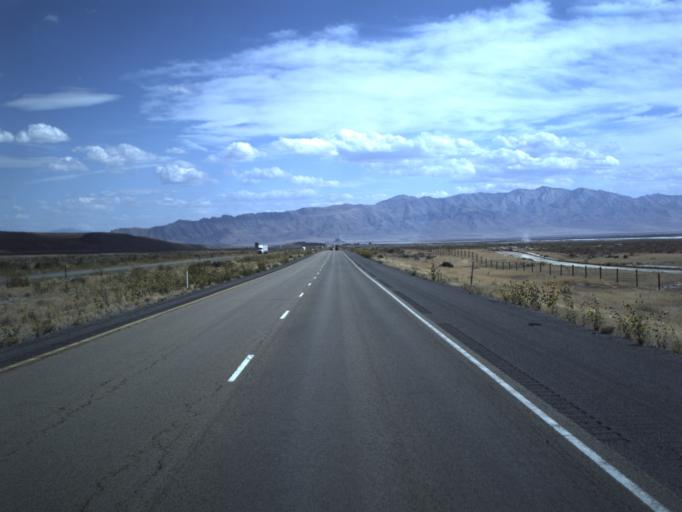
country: US
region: Utah
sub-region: Tooele County
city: Grantsville
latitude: 40.7896
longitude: -112.8307
